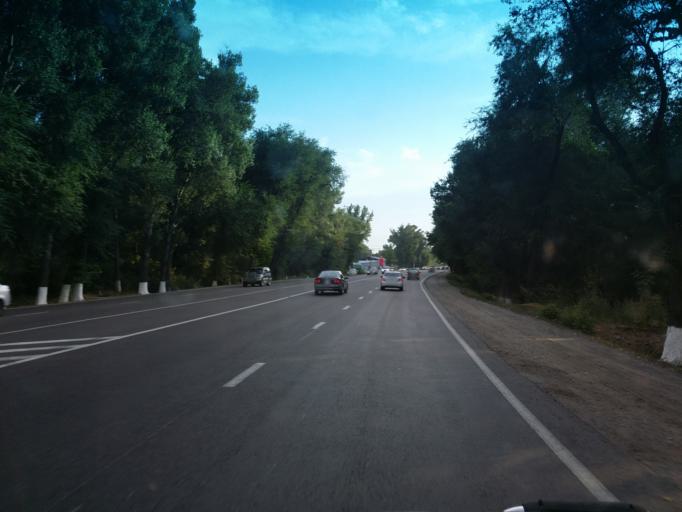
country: KZ
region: Almaty Qalasy
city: Almaty
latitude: 43.3065
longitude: 77.0138
